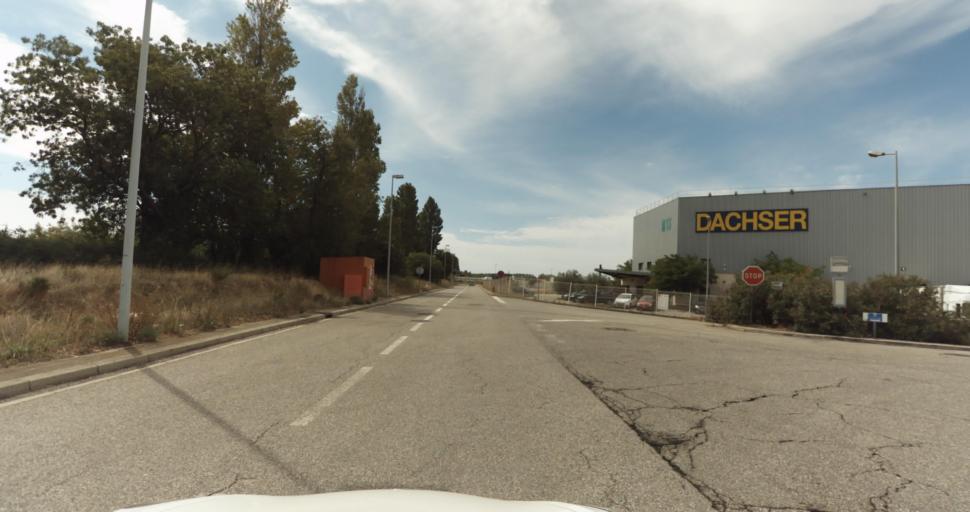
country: FR
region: Provence-Alpes-Cote d'Azur
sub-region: Departement des Bouches-du-Rhone
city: Miramas
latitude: 43.6033
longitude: 4.9992
